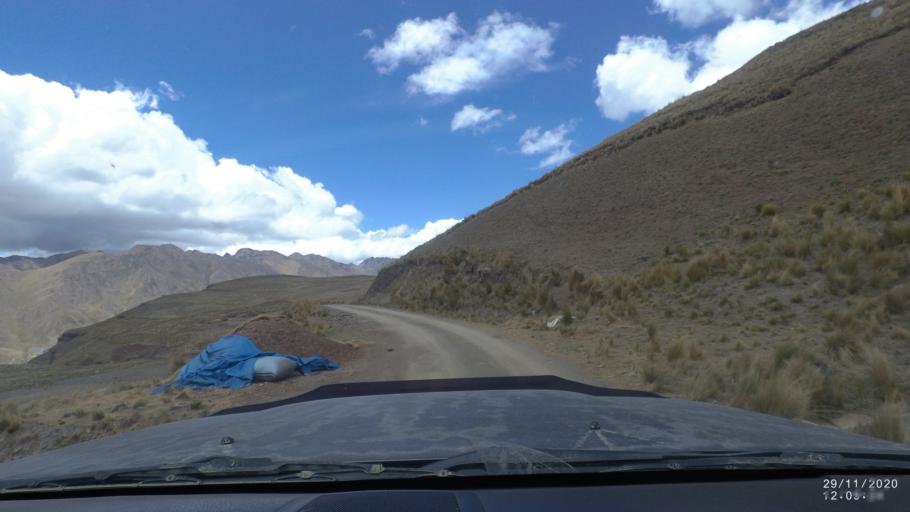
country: BO
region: Cochabamba
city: Cochabamba
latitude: -17.1307
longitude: -66.3035
